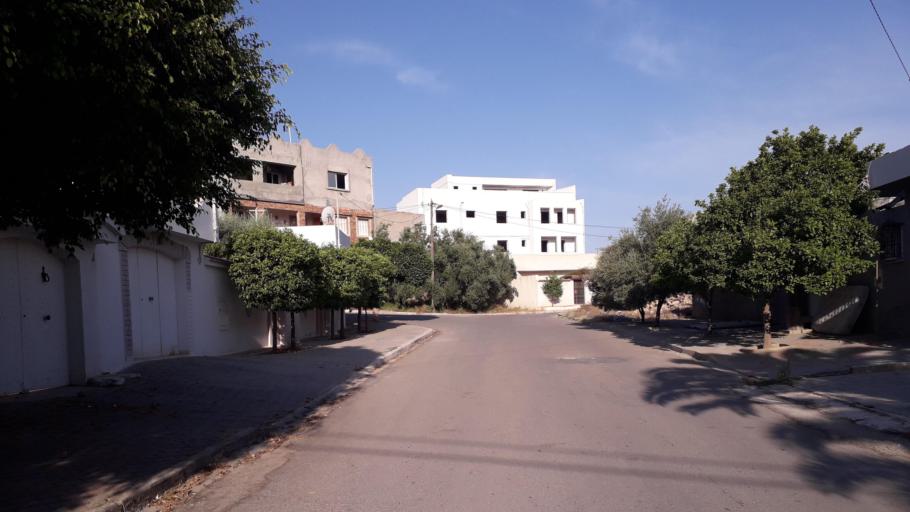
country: TN
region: Susah
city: Hammam Sousse
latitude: 35.8511
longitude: 10.5879
